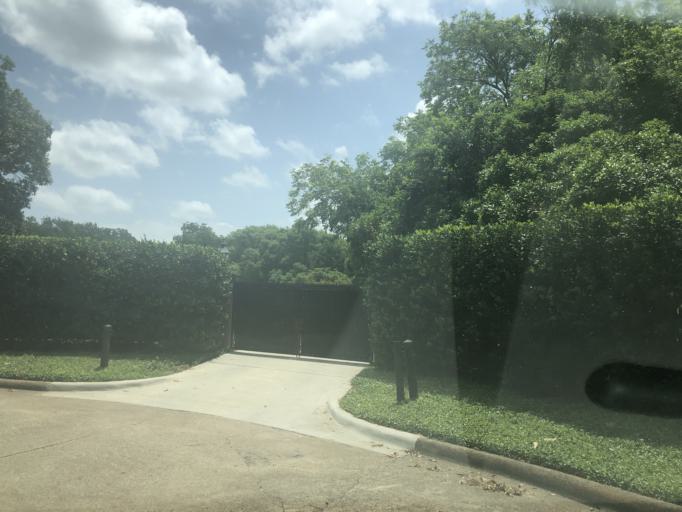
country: US
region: Texas
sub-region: Dallas County
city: University Park
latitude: 32.8901
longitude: -96.8224
